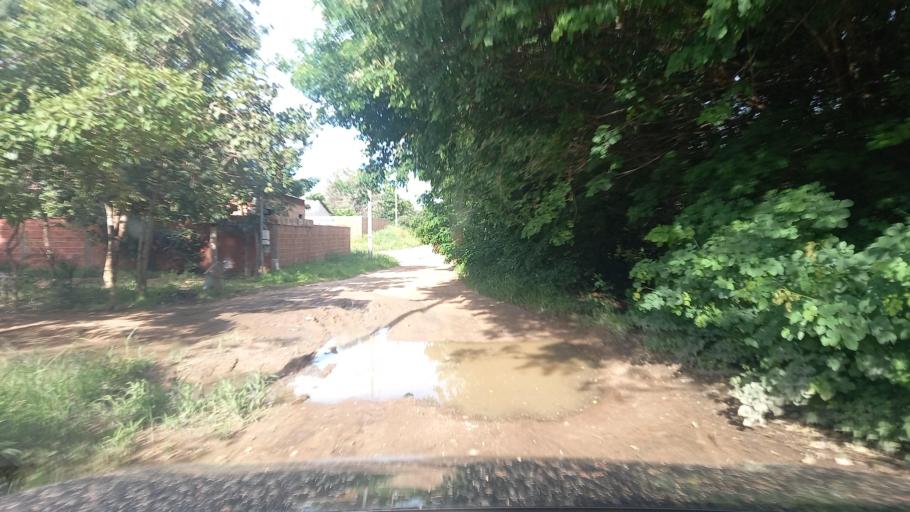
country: BR
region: Goias
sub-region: Cavalcante
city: Cavalcante
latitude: -13.8008
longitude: -47.4422
